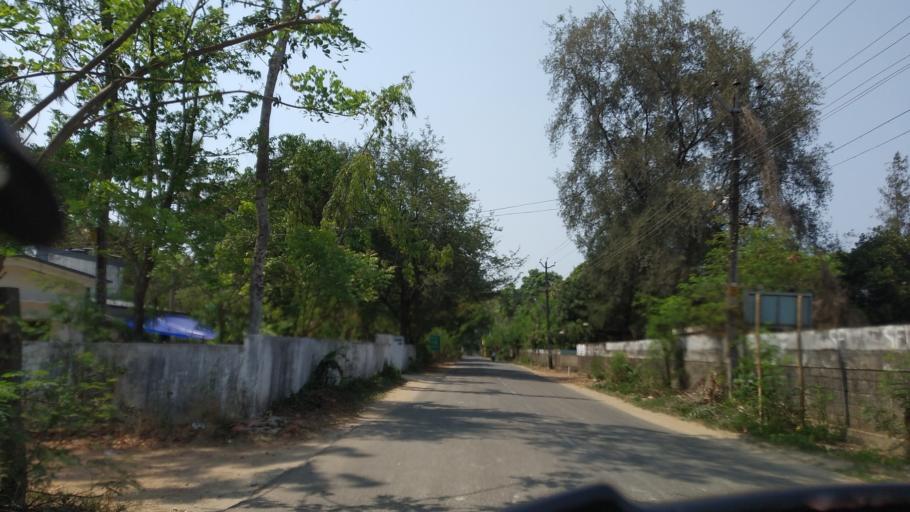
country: IN
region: Kerala
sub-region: Thrissur District
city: Kodungallur
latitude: 10.2687
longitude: 76.1414
